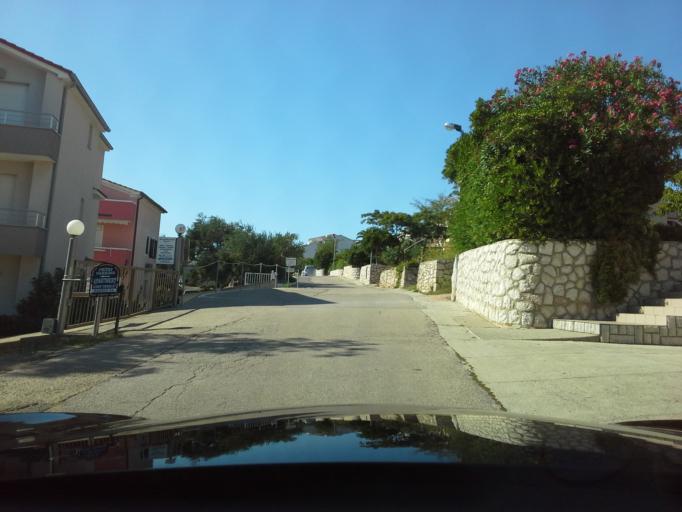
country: HR
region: Primorsko-Goranska
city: Banjol
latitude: 44.7421
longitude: 14.7944
